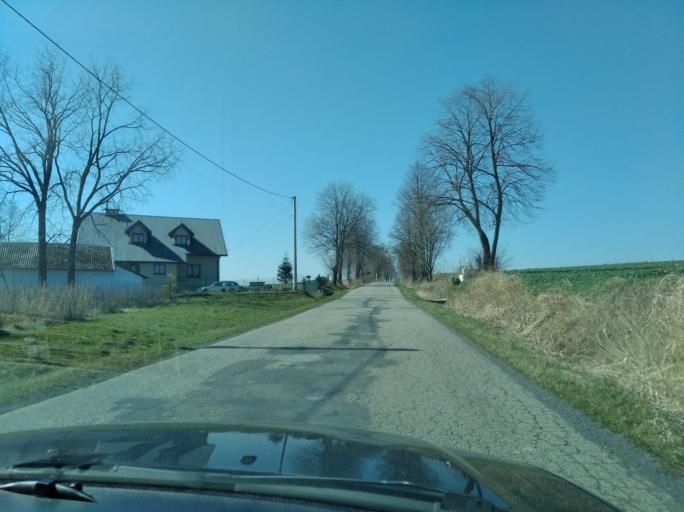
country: PL
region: Subcarpathian Voivodeship
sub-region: Powiat jaroslawski
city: Jodlowka
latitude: 49.9266
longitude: 22.4764
